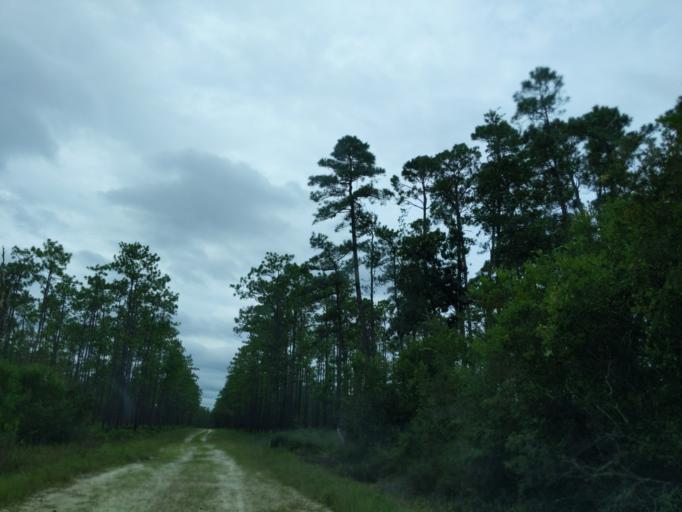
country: US
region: Florida
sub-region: Gadsden County
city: Midway
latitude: 30.3893
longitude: -84.4654
